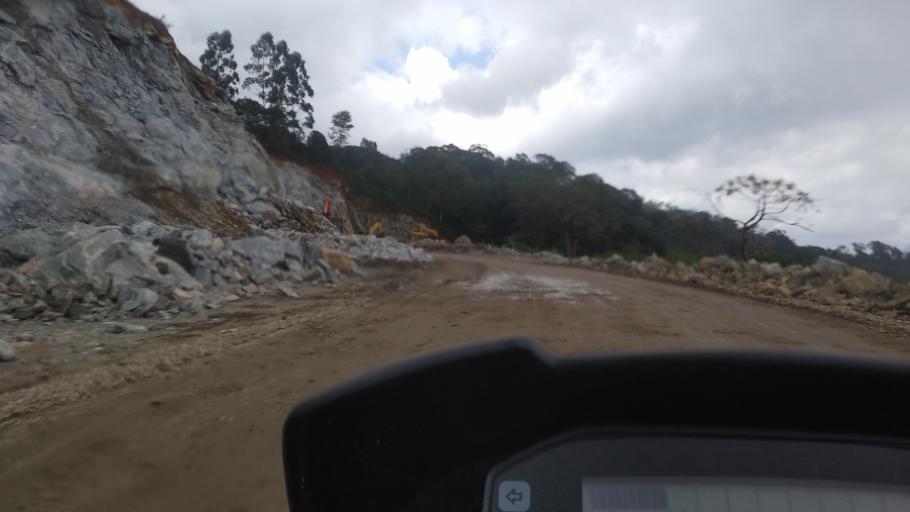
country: IN
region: Kerala
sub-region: Idukki
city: Munnar
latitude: 10.0351
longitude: 77.1425
